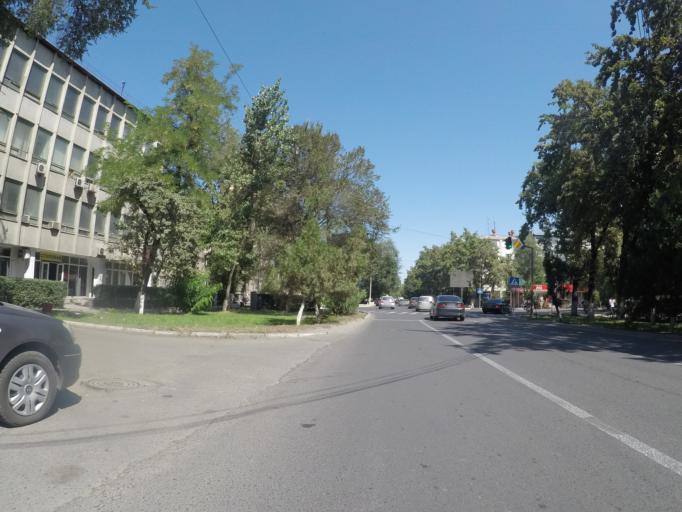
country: KG
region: Chuy
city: Bishkek
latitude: 42.8808
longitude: 74.5963
